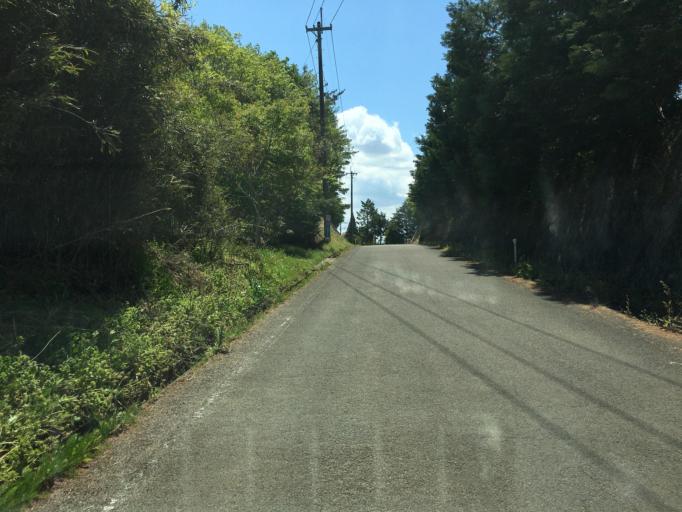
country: JP
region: Miyagi
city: Marumori
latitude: 37.8107
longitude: 140.9494
